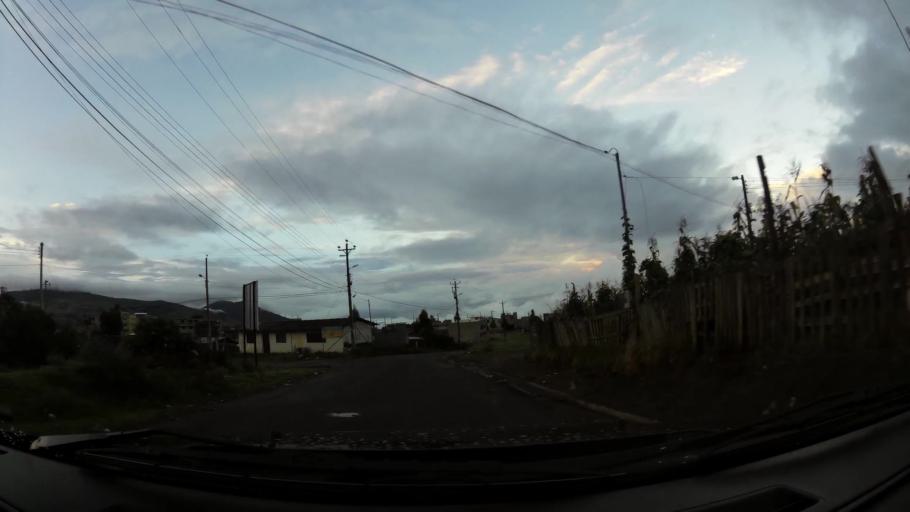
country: EC
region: Pichincha
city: Quito
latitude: -0.0962
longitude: -78.5289
